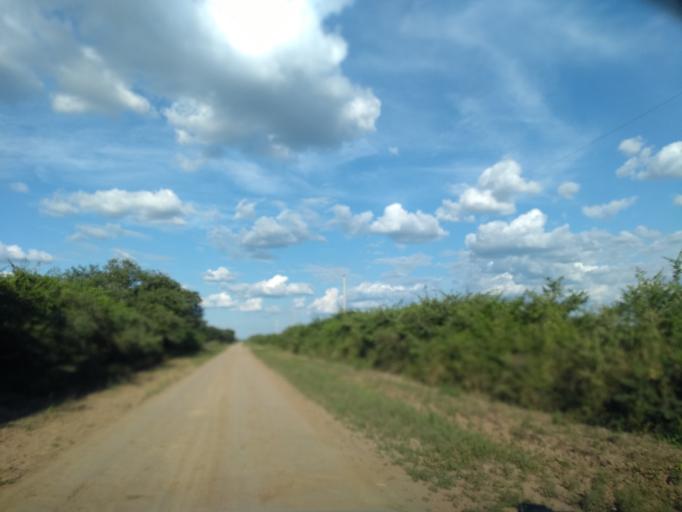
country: AR
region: Chaco
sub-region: Departamento de Quitilipi
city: Quitilipi
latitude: -26.7698
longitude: -60.2068
